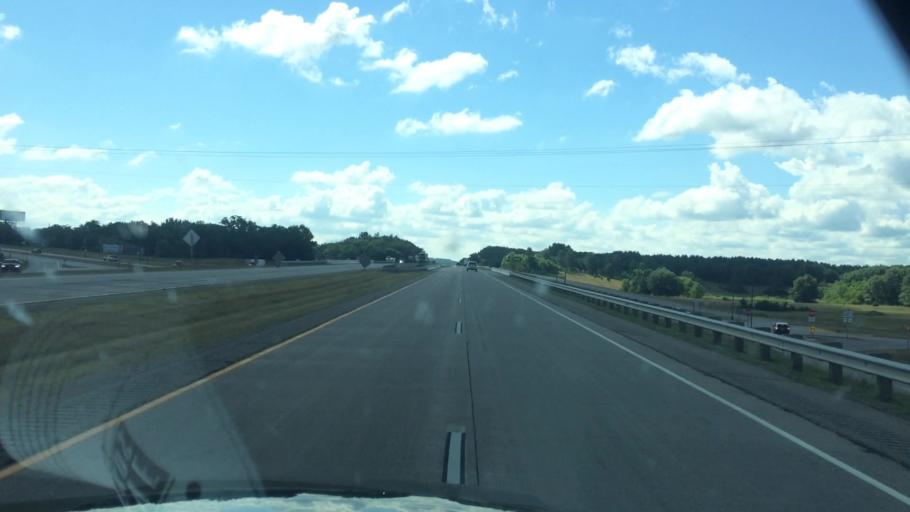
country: US
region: Wisconsin
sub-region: Waupaca County
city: Waupaca
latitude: 44.3574
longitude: -89.1171
